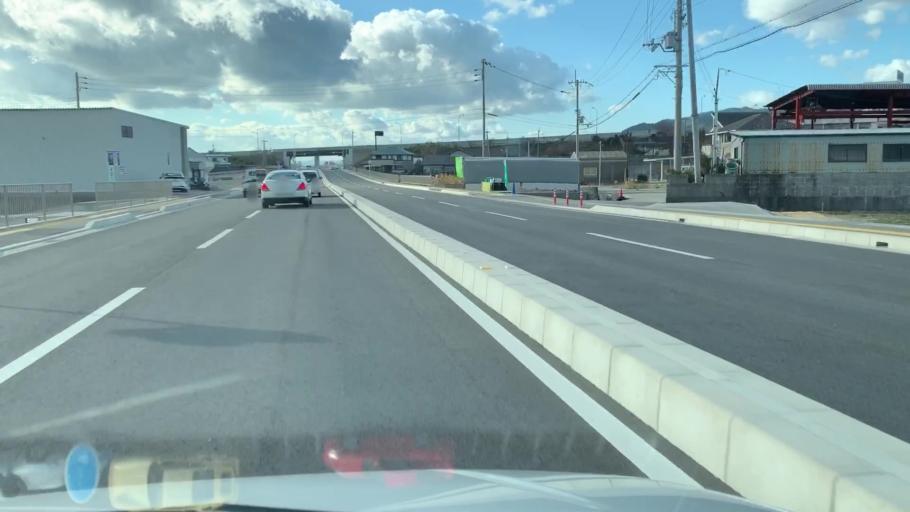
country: JP
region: Wakayama
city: Wakayama-shi
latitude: 34.2618
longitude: 135.2266
